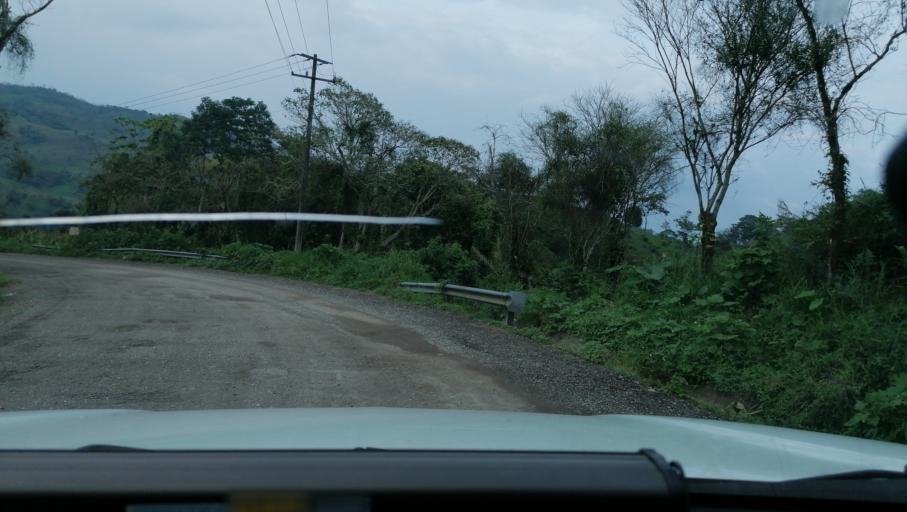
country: MX
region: Chiapas
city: Ixtacomitan
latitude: 17.3464
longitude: -93.1309
